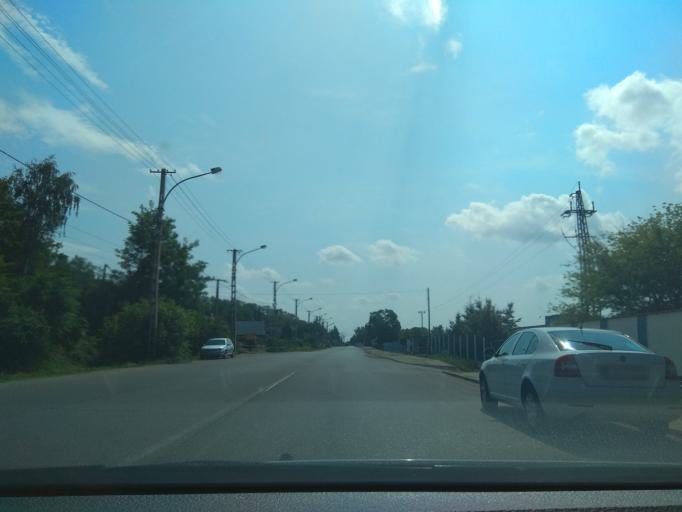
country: HU
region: Heves
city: Eger
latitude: 47.8846
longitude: 20.3981
